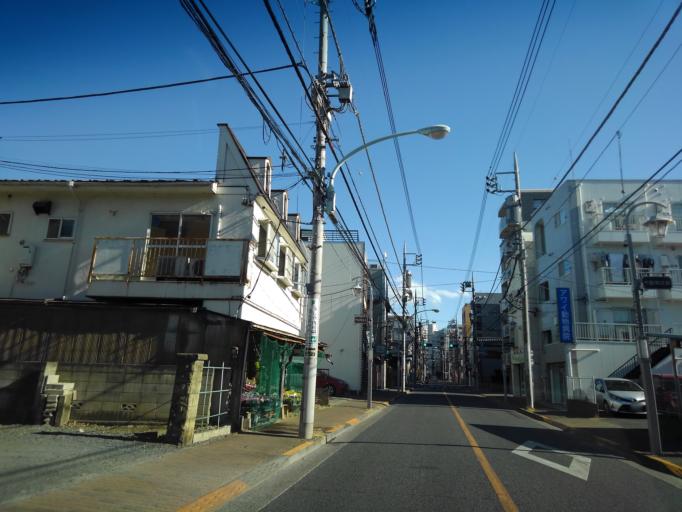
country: JP
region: Tokyo
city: Chofugaoka
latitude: 35.6509
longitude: 139.5523
